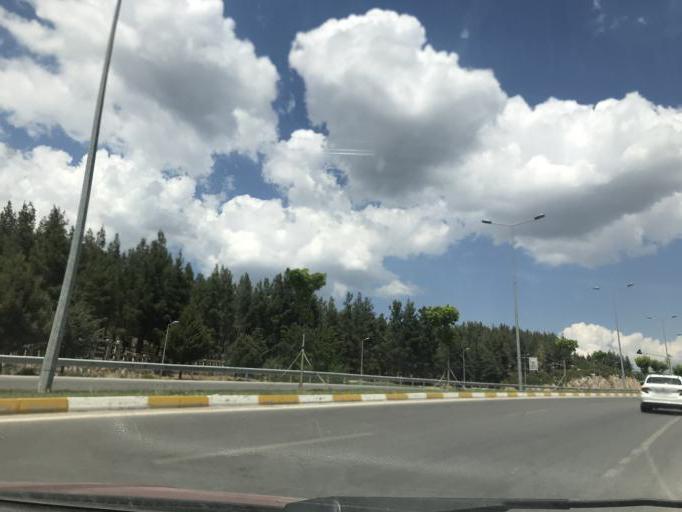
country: TR
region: Denizli
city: Tavas
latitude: 37.5726
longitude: 29.0808
